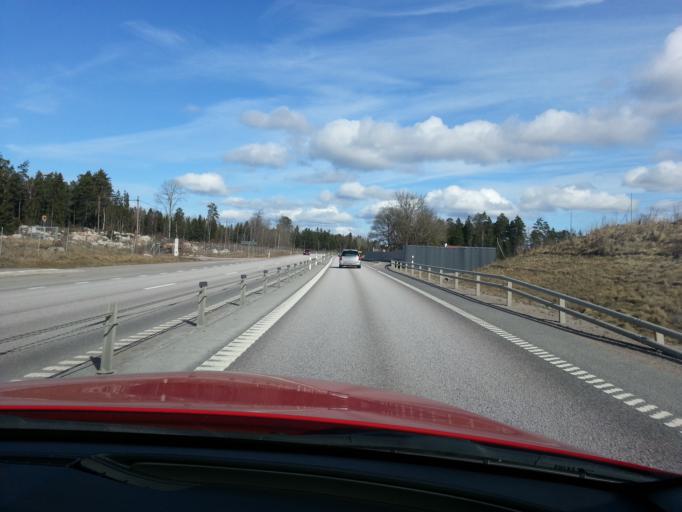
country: SE
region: Uppsala
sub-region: Uppsala Kommun
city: Storvreta
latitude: 59.9187
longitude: 17.7581
